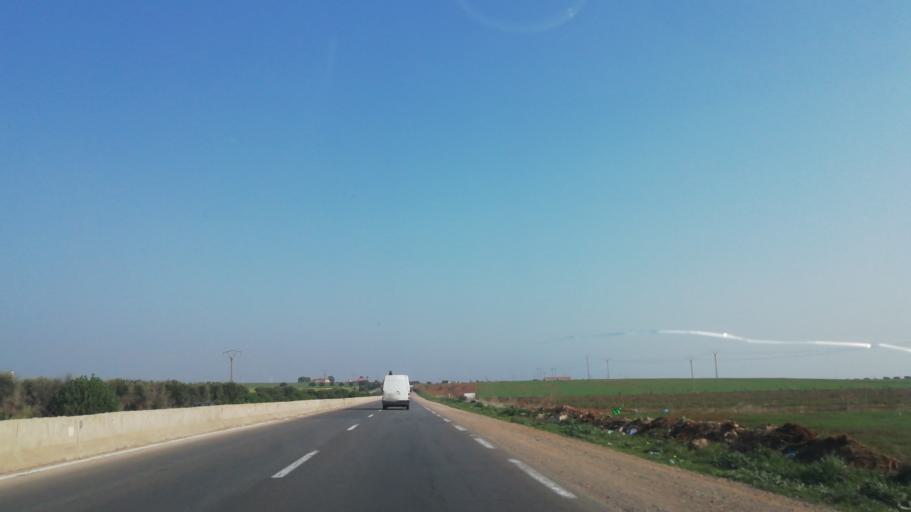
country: DZ
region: Oran
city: Bou Tlelis
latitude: 35.5528
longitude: -0.9488
